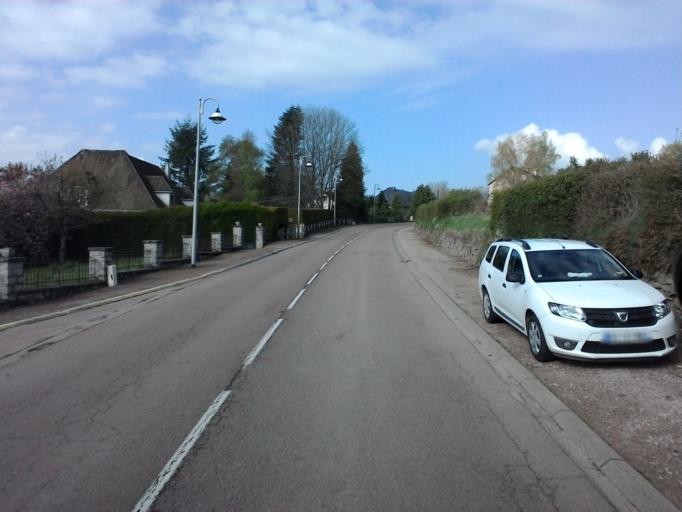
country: FR
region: Bourgogne
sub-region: Departement de la Nievre
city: Chateau-Chinon(Ville)
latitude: 47.2149
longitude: 4.0316
